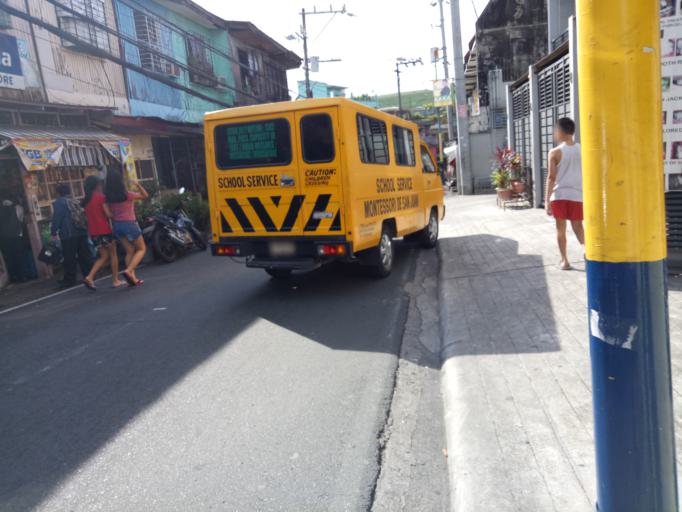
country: PH
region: Metro Manila
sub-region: San Juan
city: San Juan
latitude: 14.5905
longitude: 121.0273
